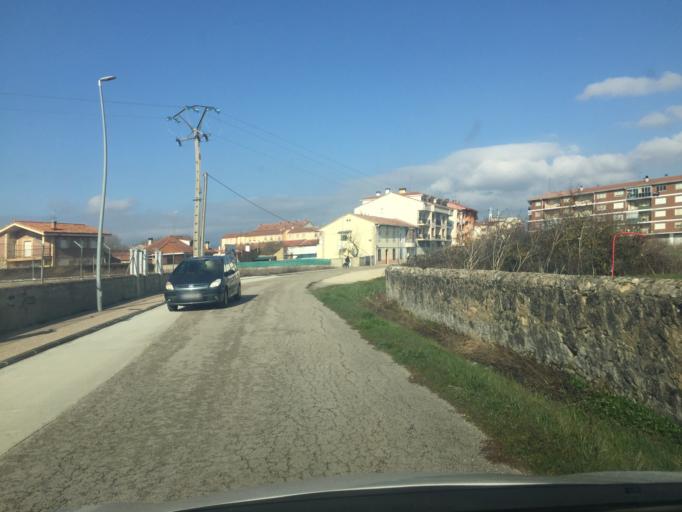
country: ES
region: Castille and Leon
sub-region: Provincia de Burgos
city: Medina de Pomar
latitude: 42.9354
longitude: -3.5762
